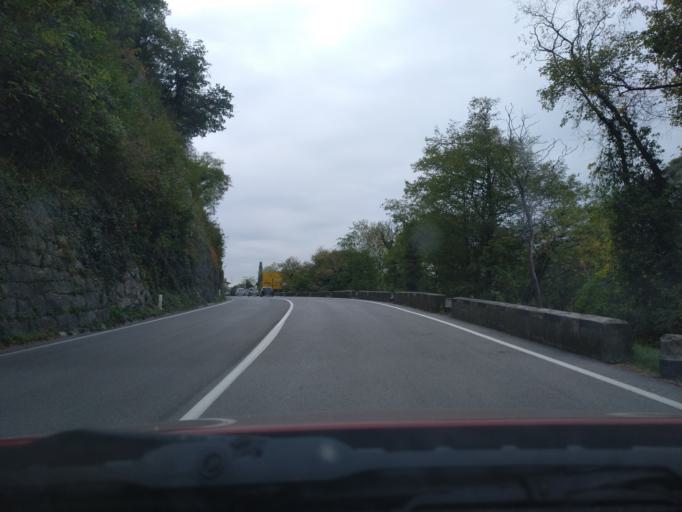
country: SI
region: Nova Gorica
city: Solkan
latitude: 45.9784
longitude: 13.6531
